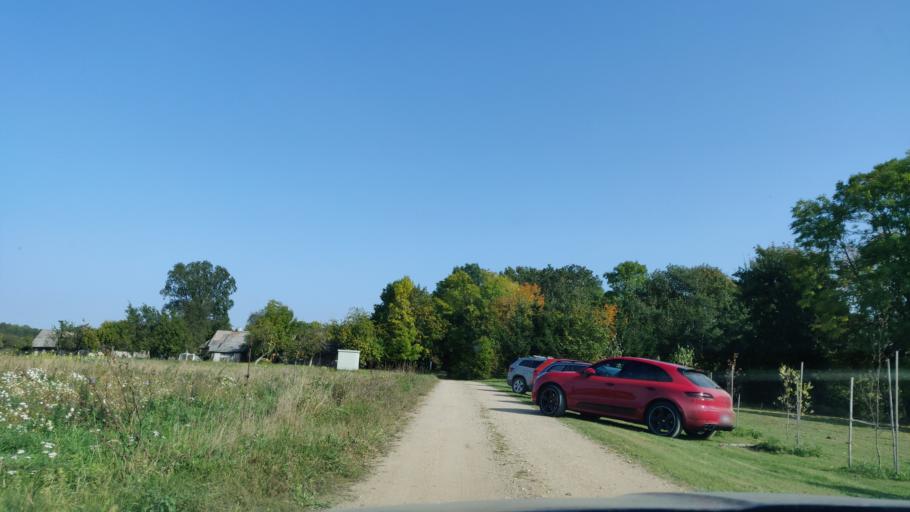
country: LT
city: Sirvintos
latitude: 54.9603
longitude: 24.7791
